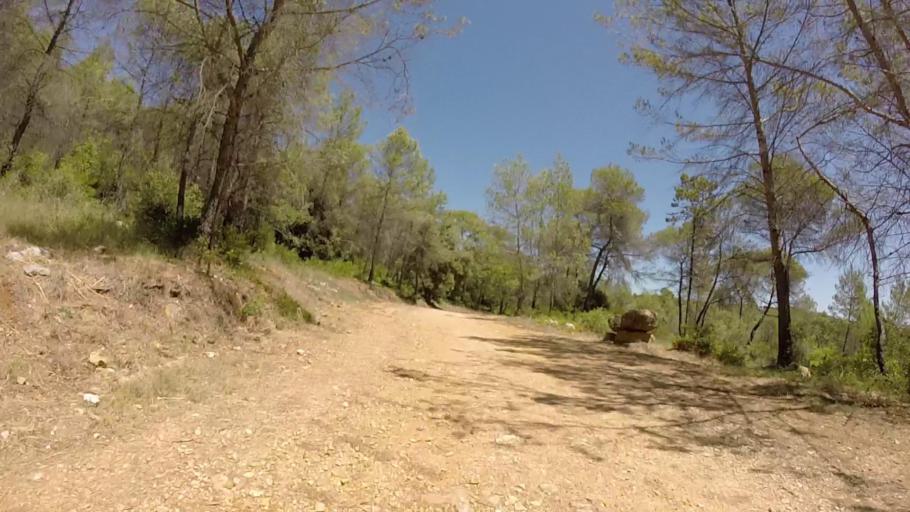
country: FR
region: Provence-Alpes-Cote d'Azur
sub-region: Departement des Alpes-Maritimes
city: Valbonne
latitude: 43.6340
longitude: 7.0406
